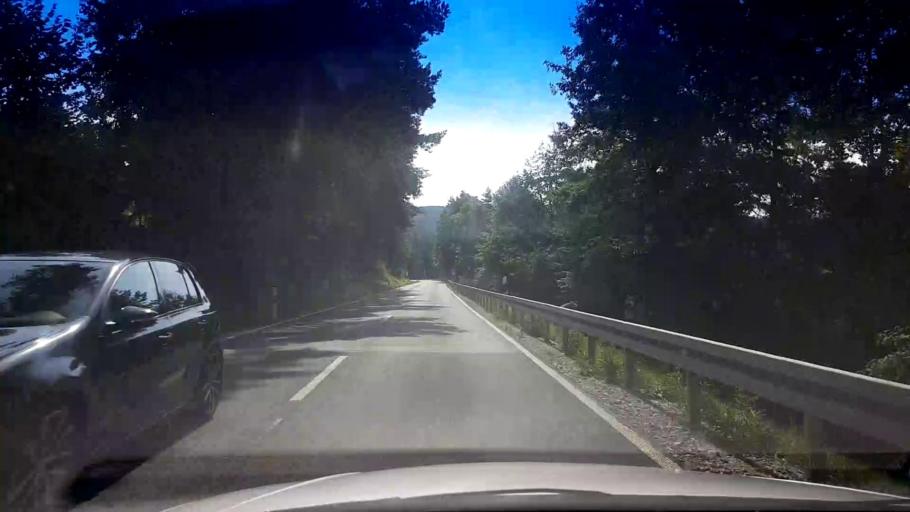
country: DE
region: Bavaria
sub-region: Upper Franconia
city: Plankenfels
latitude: 49.9343
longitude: 11.3793
